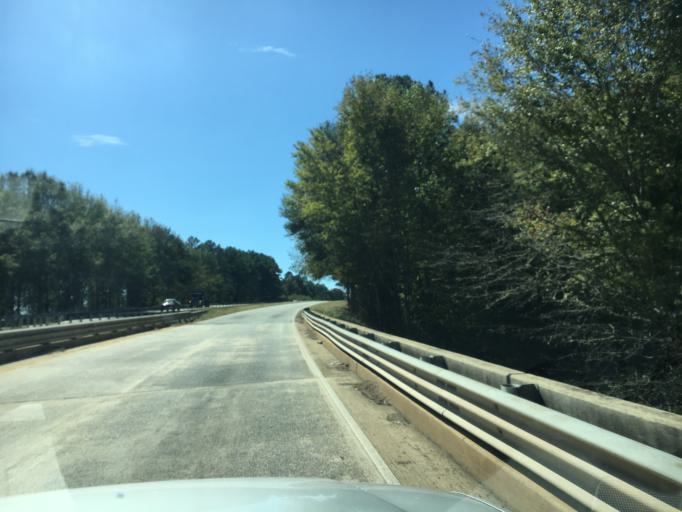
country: US
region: South Carolina
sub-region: Pickens County
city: Liberty
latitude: 34.7678
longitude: -82.6748
